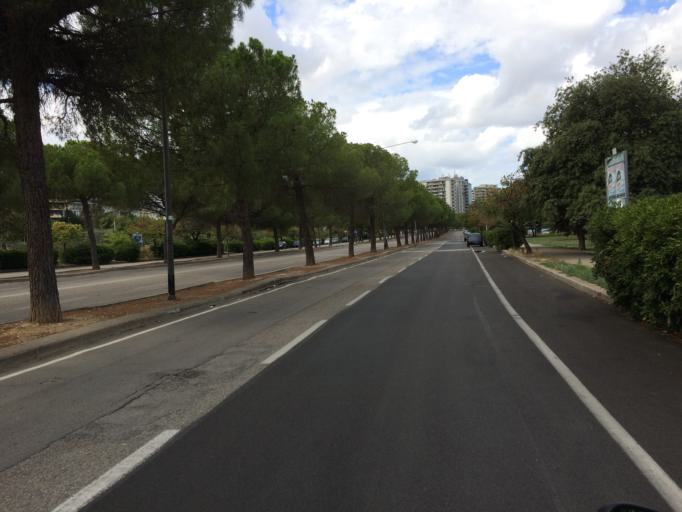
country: IT
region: Apulia
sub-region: Provincia di Bari
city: Bari
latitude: 41.0991
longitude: 16.8623
